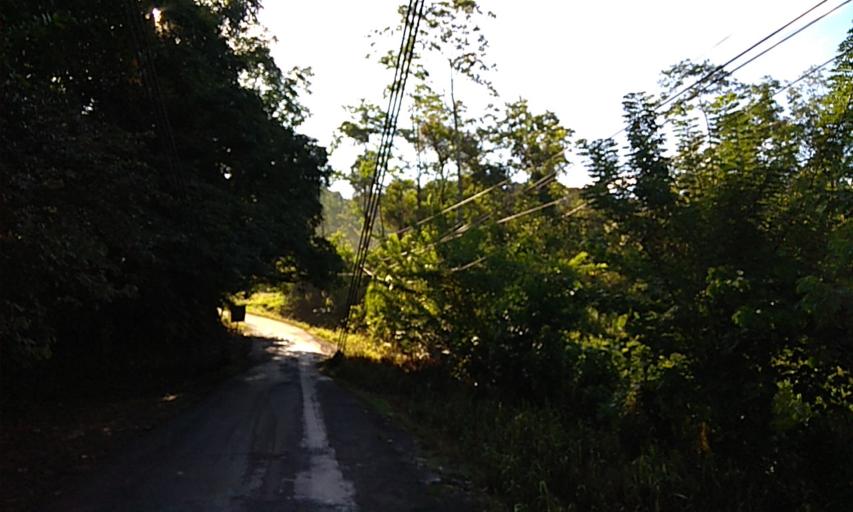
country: CR
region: Limon
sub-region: Canton de Pococi
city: Guapiles
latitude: 10.1634
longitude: -83.8044
